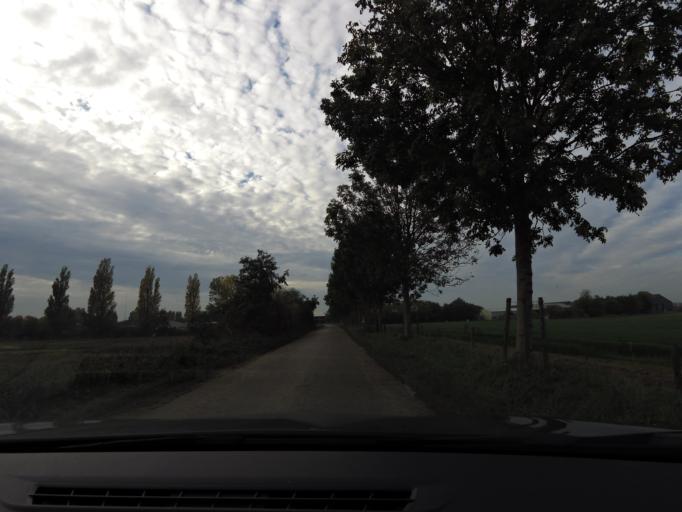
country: NL
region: South Holland
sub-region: Gemeente Goeree-Overflakkee
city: Middelharnis
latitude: 51.7195
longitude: 4.1799
